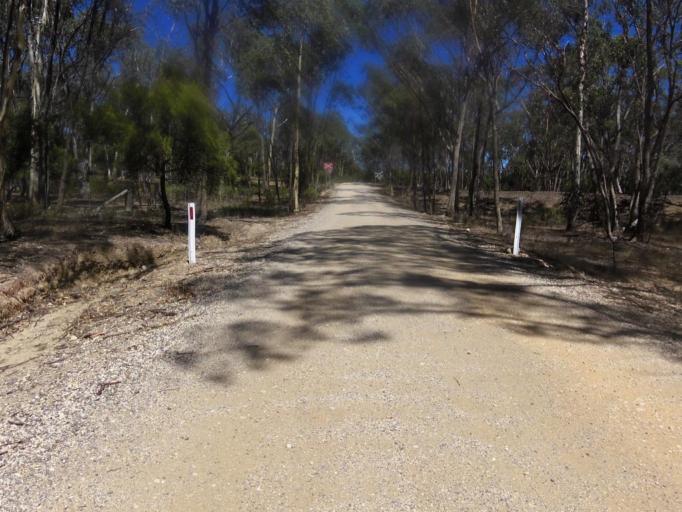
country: AU
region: Victoria
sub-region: Mount Alexander
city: Castlemaine
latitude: -37.0460
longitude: 144.1817
